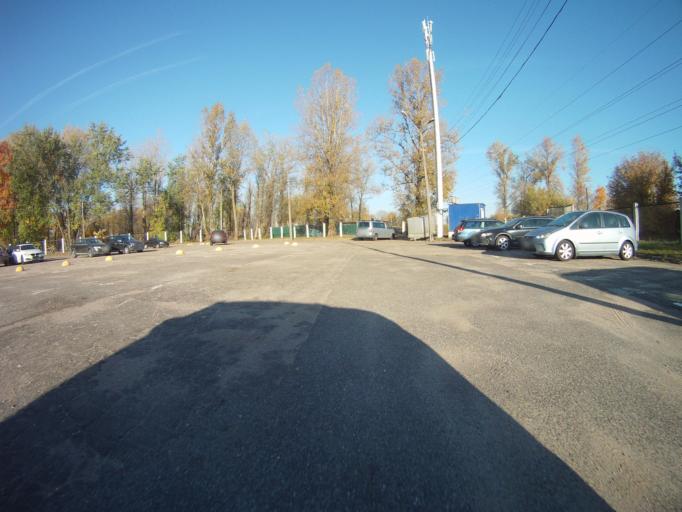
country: BY
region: Minsk
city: Minsk
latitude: 53.9423
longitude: 27.5650
